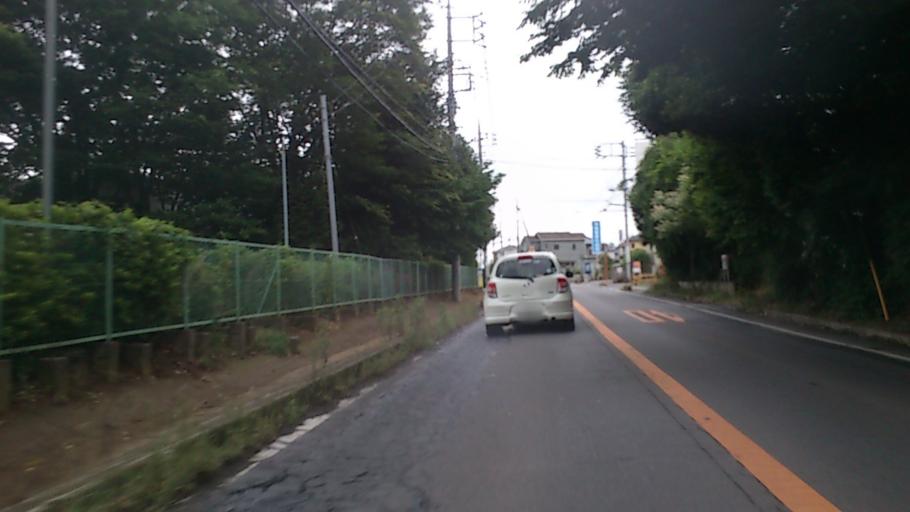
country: JP
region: Ibaraki
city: Ami
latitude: 36.0241
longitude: 140.2199
